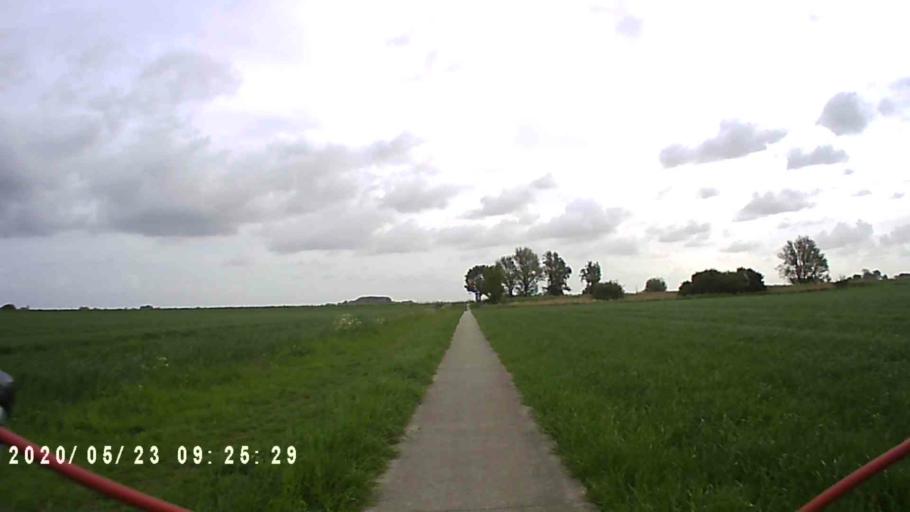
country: NL
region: Groningen
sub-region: Gemeente Bedum
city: Bedum
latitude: 53.2941
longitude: 6.6913
